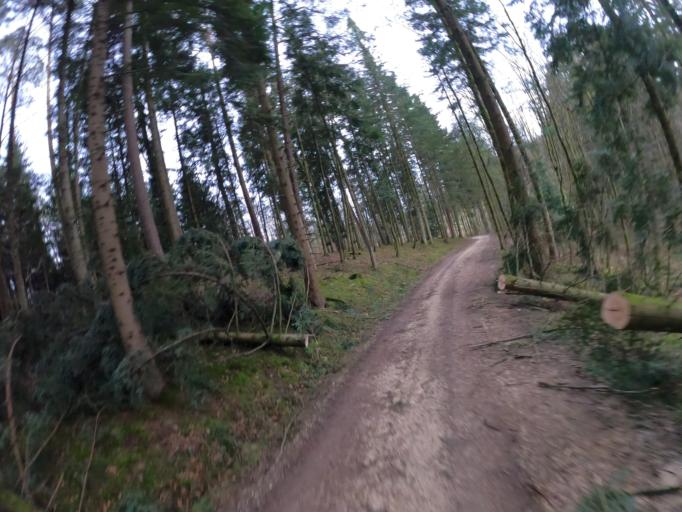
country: DE
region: Baden-Wuerttemberg
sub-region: Regierungsbezirk Stuttgart
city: Ottenbach
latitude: 48.7329
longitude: 9.7284
